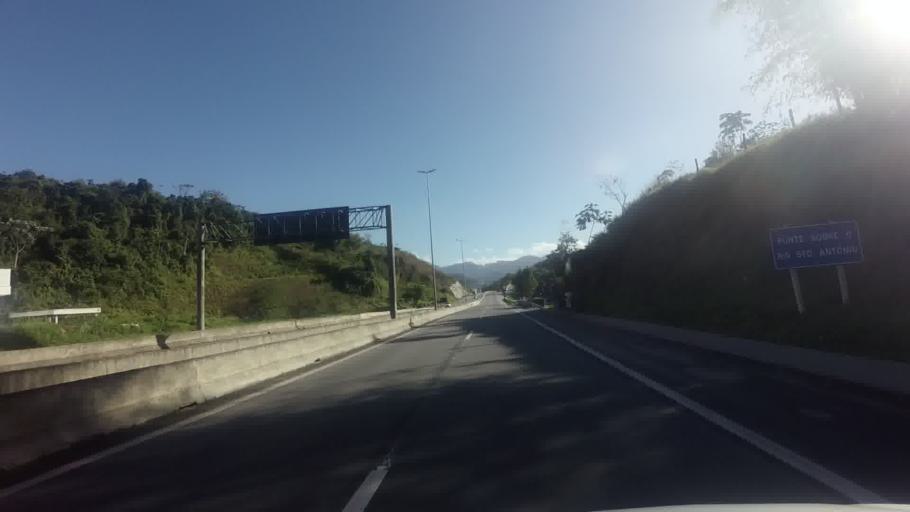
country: BR
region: Rio de Janeiro
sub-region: Petropolis
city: Petropolis
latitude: -22.6061
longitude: -43.2852
